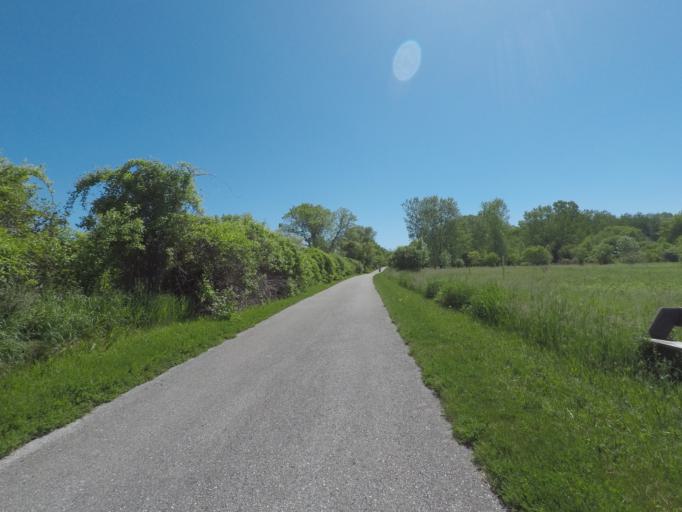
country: US
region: Wisconsin
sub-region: Sheboygan County
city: Kohler
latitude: 43.7530
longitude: -87.7759
